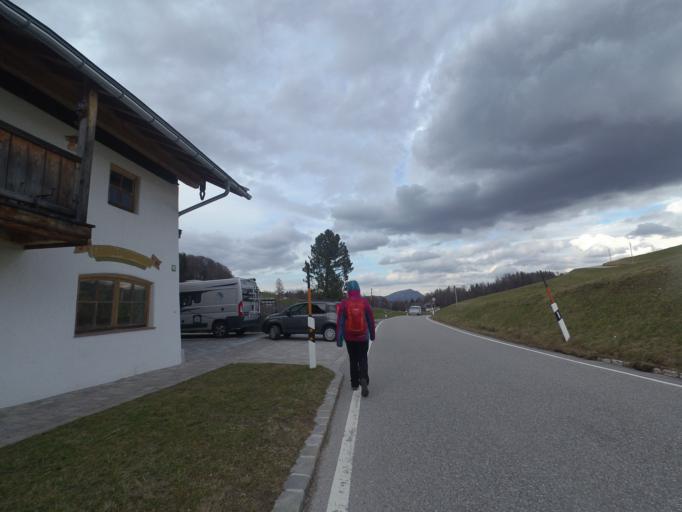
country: AT
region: Salzburg
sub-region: Politischer Bezirk Hallein
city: Hallein
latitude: 47.6635
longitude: 13.0770
